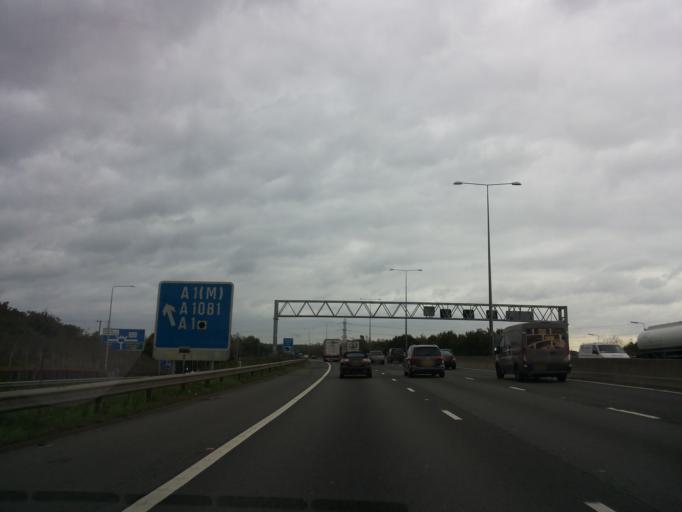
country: GB
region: England
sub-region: Greater London
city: High Barnet
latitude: 51.6889
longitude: -0.2331
